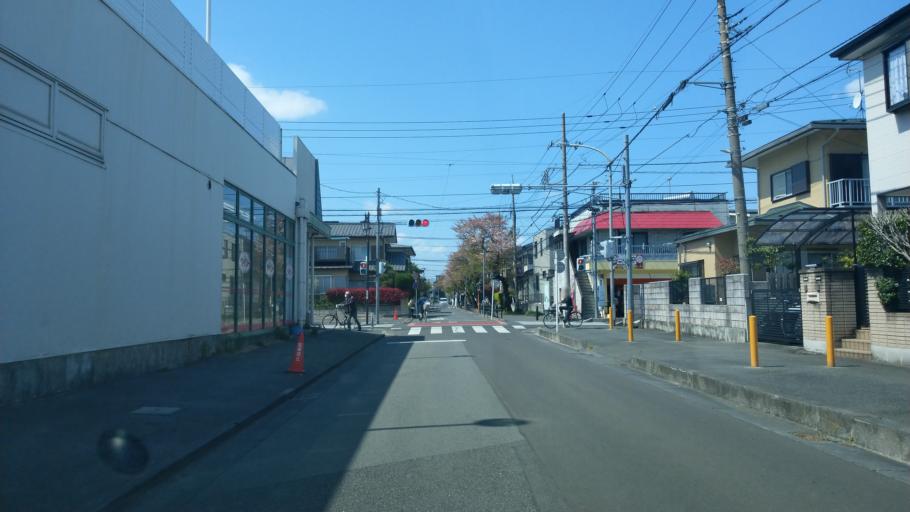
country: JP
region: Saitama
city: Yono
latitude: 35.8859
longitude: 139.6068
